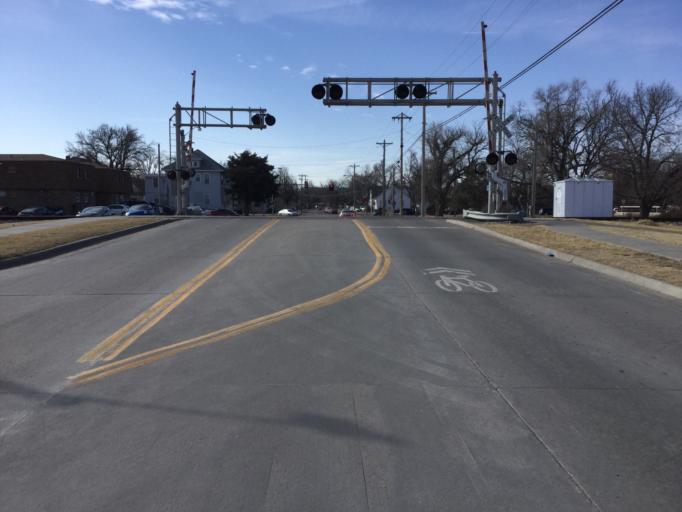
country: US
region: Kansas
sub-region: Ellis County
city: Hays
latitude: 38.8743
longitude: -99.3371
